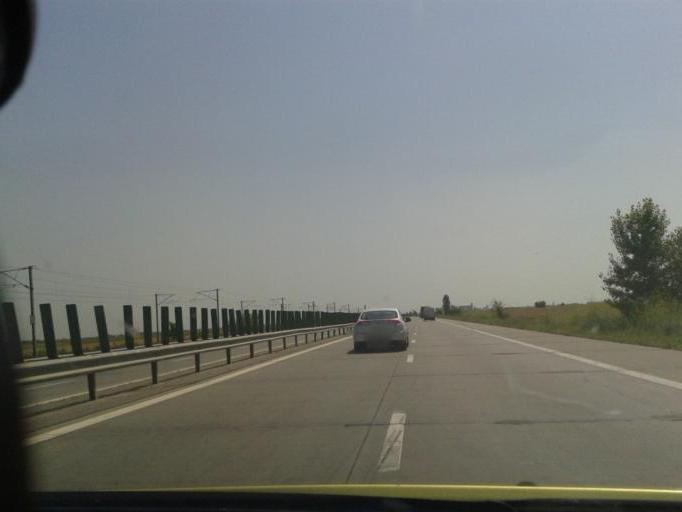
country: RO
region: Calarasi
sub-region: Comuna Belciugatele
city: Belciugatele
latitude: 44.4554
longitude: 26.4666
